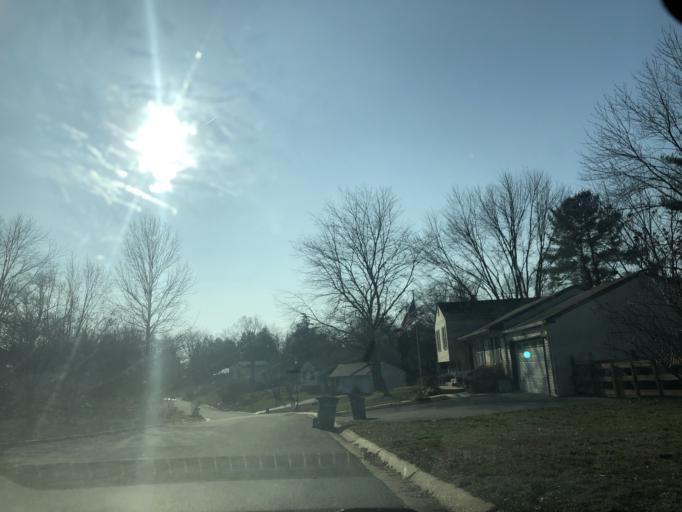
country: US
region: Maryland
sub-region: Montgomery County
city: Burtonsville
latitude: 39.1026
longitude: -76.9383
